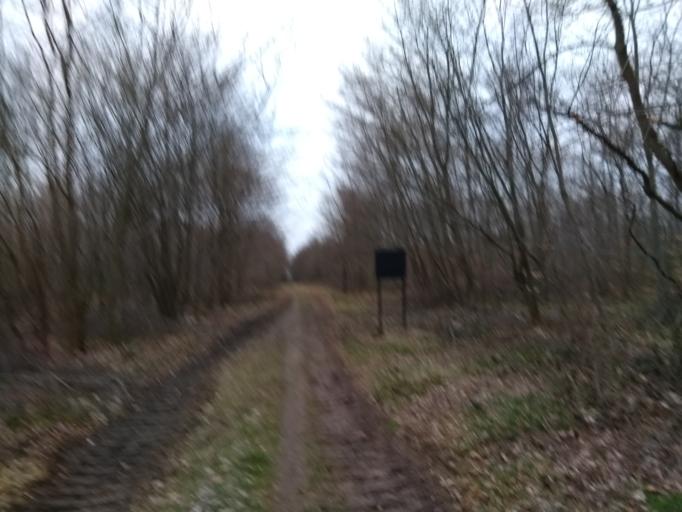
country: FR
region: Picardie
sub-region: Departement de l'Oise
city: Choisy-au-Bac
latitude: 49.4394
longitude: 2.8966
